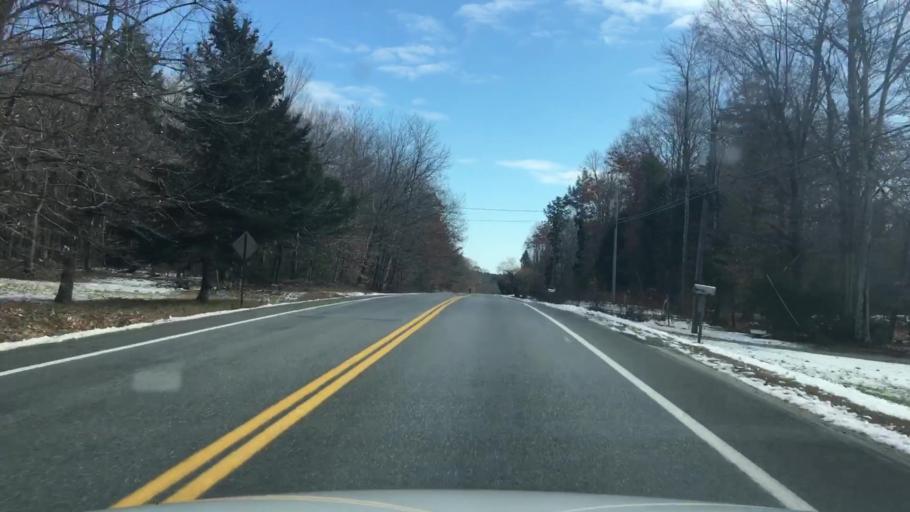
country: US
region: Maine
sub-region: Kennebec County
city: Winthrop
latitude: 44.3283
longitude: -69.9991
